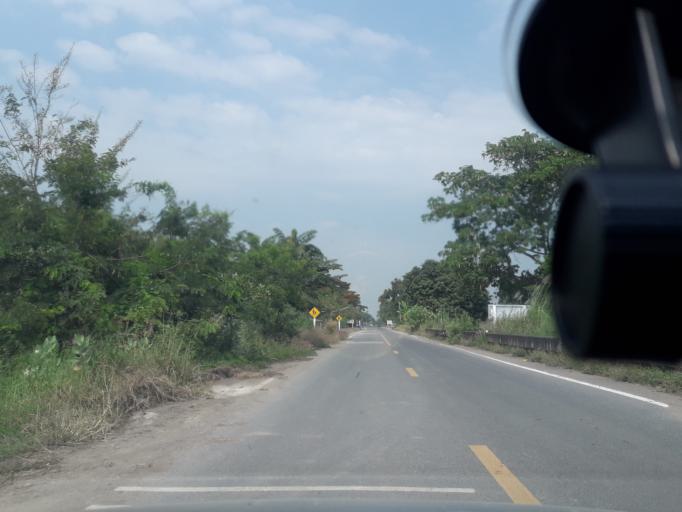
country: TH
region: Pathum Thani
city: Nong Suea
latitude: 14.2181
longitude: 100.8914
